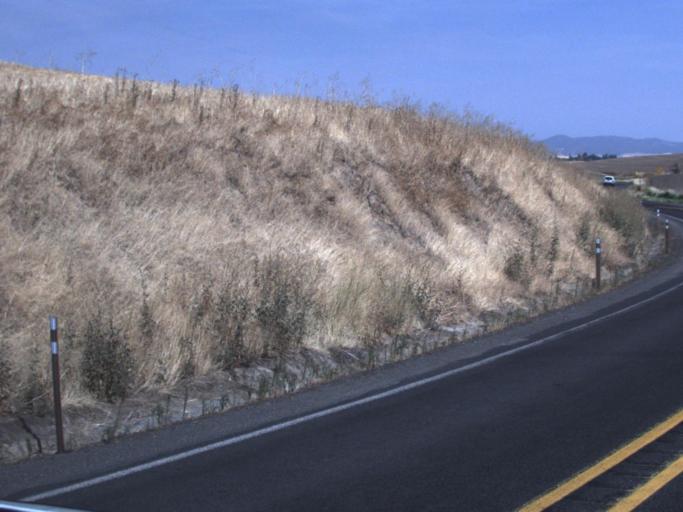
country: US
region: Idaho
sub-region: Benewah County
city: Plummer
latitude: 47.1961
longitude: -117.0973
